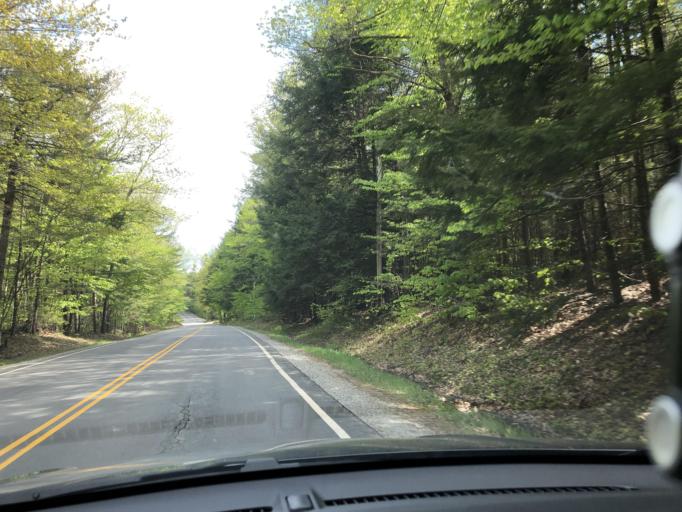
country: US
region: New Hampshire
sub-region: Merrimack County
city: New London
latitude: 43.4172
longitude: -72.0360
